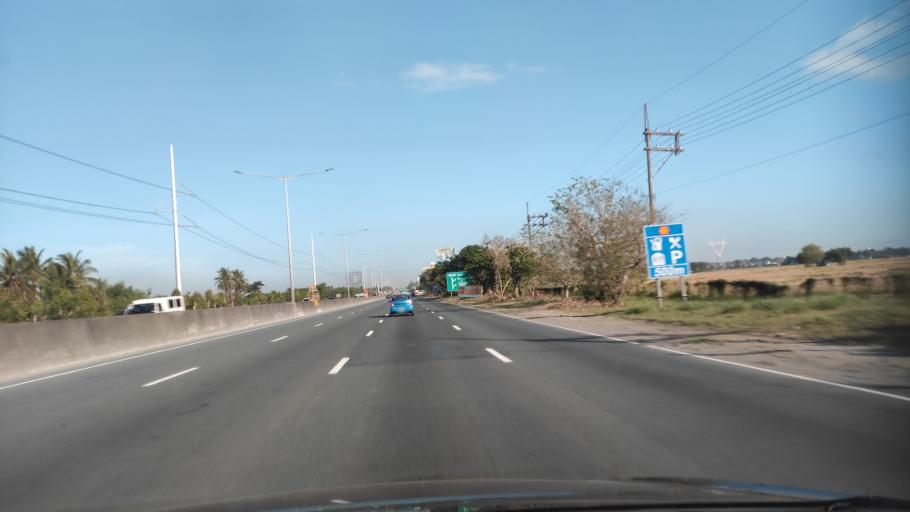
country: PH
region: Central Luzon
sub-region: Province of Bulacan
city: Guiguinto
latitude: 14.8278
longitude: 120.9142
